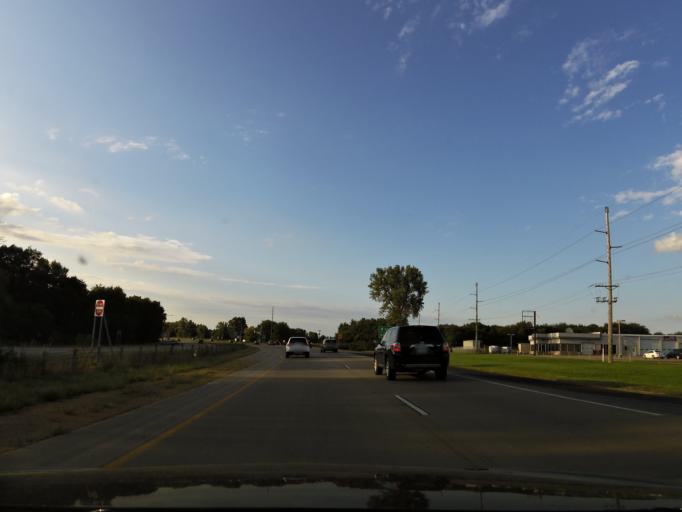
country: US
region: Minnesota
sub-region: Dakota County
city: Hastings
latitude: 44.7755
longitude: -92.8631
